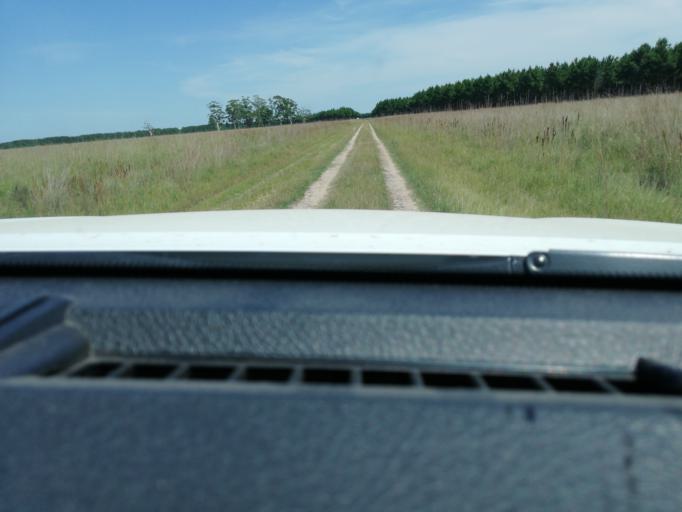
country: AR
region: Corrientes
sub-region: Departamento de San Miguel
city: San Miguel
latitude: -28.0393
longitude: -57.4619
